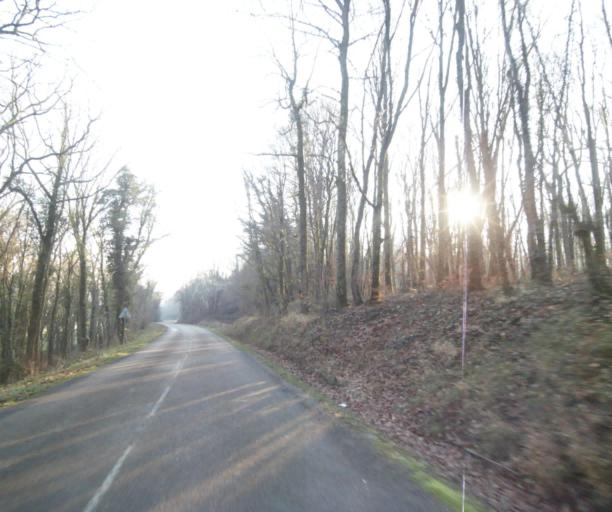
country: FR
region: Champagne-Ardenne
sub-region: Departement de la Haute-Marne
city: Bienville
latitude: 48.5713
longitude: 5.0784
